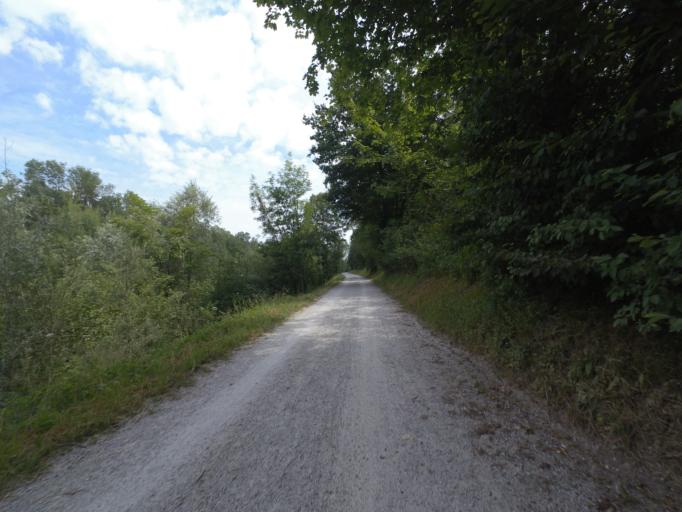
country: DE
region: Bavaria
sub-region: Upper Bavaria
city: Ainring
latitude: 47.7998
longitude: 12.9645
